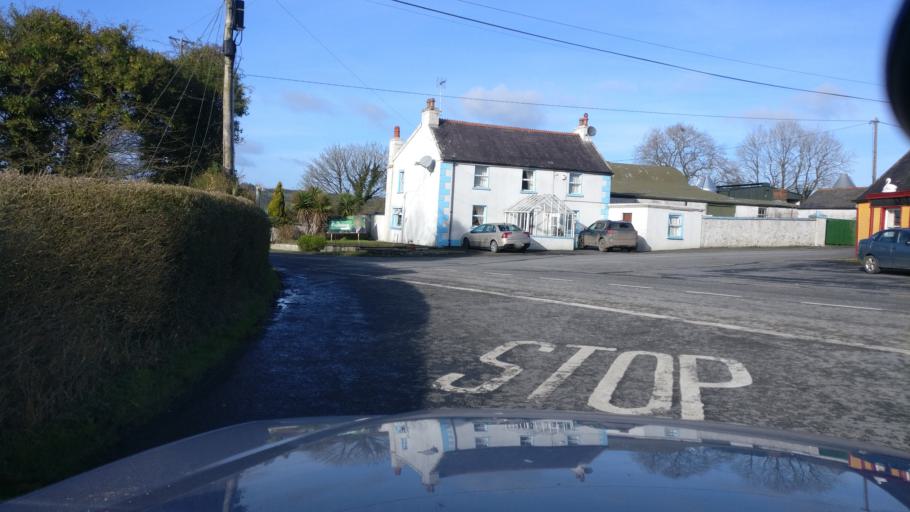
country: IE
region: Leinster
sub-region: Kilkenny
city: Castlecomer
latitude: 52.8889
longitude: -7.1605
